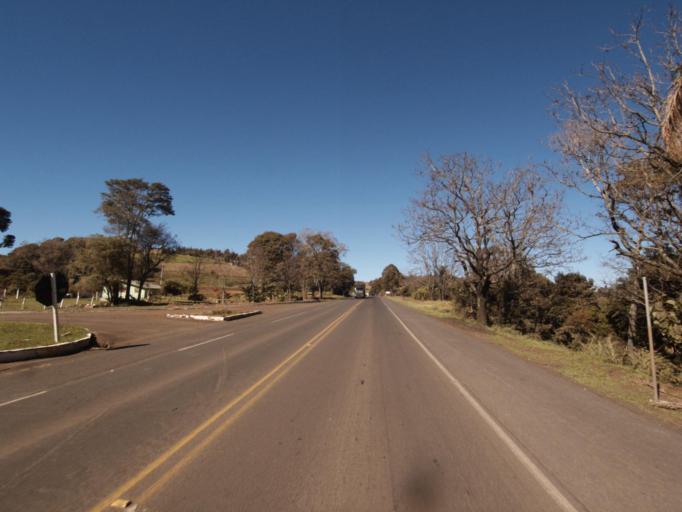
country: BR
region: Santa Catarina
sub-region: Chapeco
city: Chapeco
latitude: -26.9714
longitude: -52.7495
